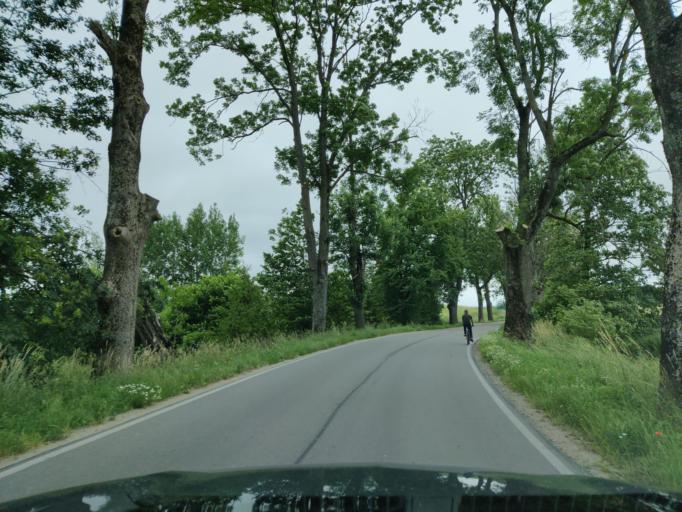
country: PL
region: Warmian-Masurian Voivodeship
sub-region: Powiat mragowski
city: Mikolajki
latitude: 53.8745
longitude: 21.5944
